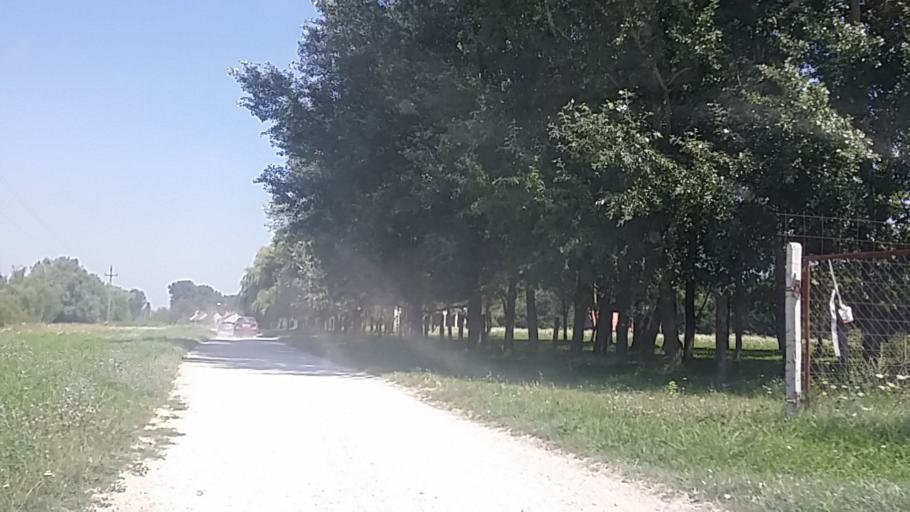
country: HU
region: Zala
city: Keszthely
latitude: 46.6995
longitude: 17.2379
